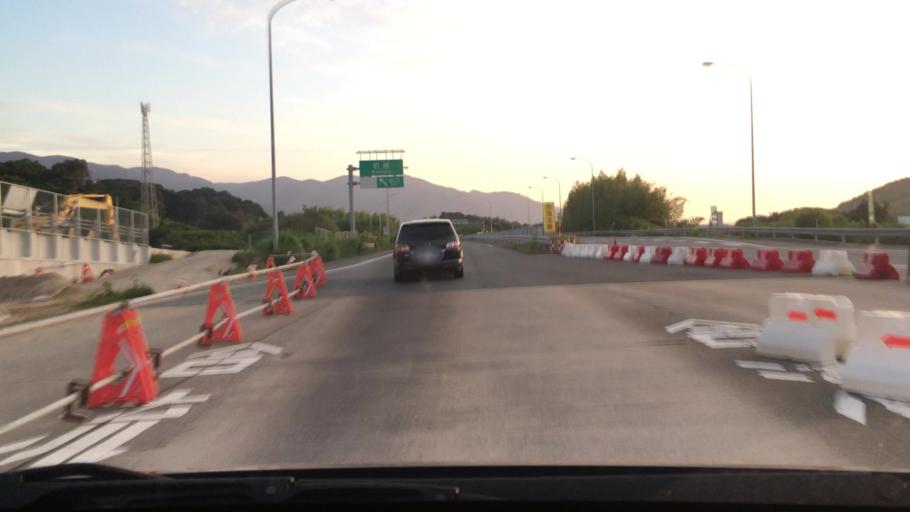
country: JP
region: Fukuoka
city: Maebaru-chuo
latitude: 33.5422
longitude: 130.2018
